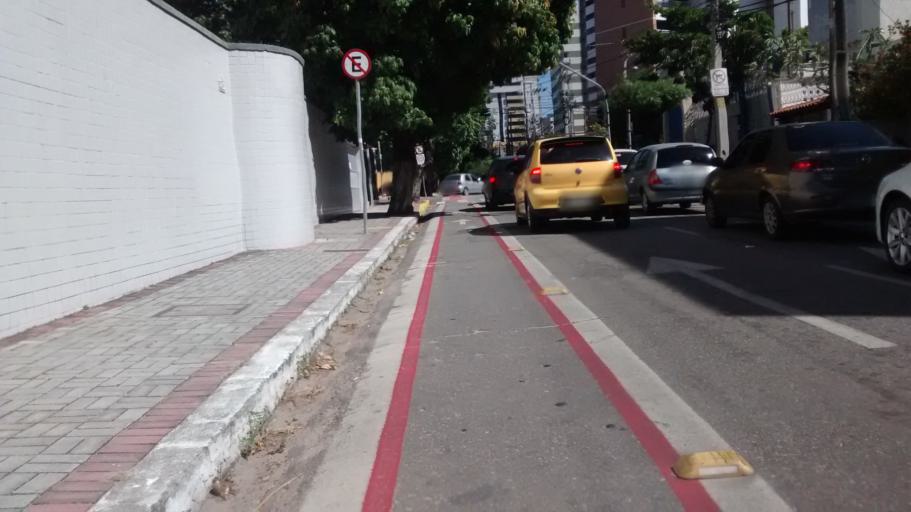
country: BR
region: Ceara
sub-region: Fortaleza
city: Fortaleza
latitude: -3.7430
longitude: -38.5027
